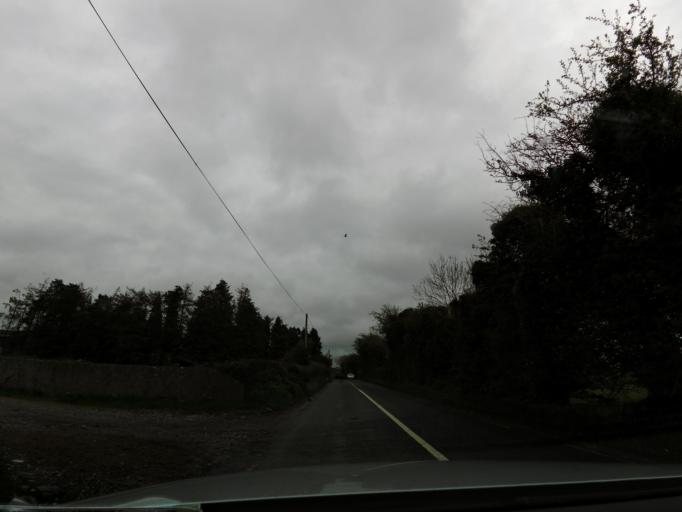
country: IE
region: Leinster
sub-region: Laois
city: Rathdowney
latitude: 52.7230
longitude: -7.5533
